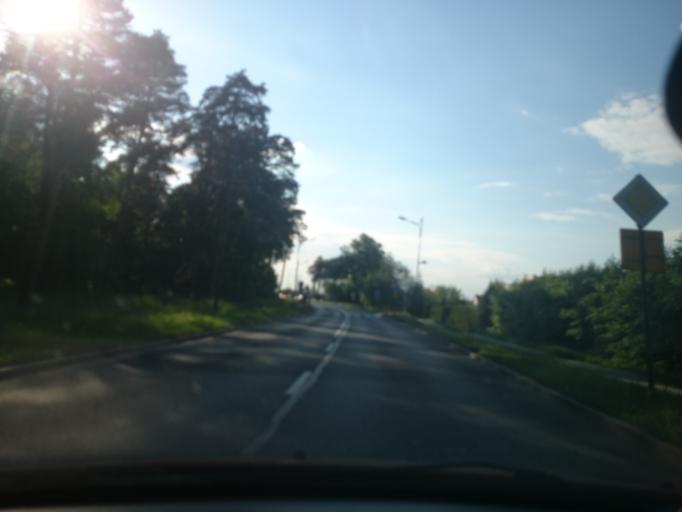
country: PL
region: Opole Voivodeship
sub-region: Powiat strzelecki
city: Strzelce Opolskie
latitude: 50.5194
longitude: 18.2848
